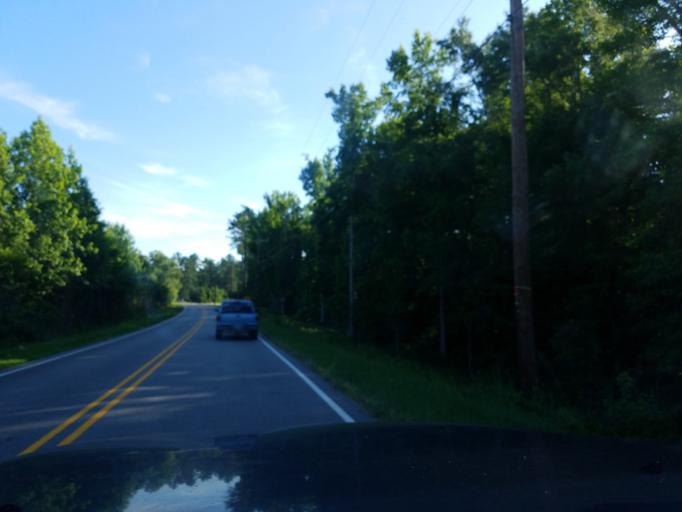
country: US
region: North Carolina
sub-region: Granville County
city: Butner
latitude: 36.1567
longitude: -78.7655
